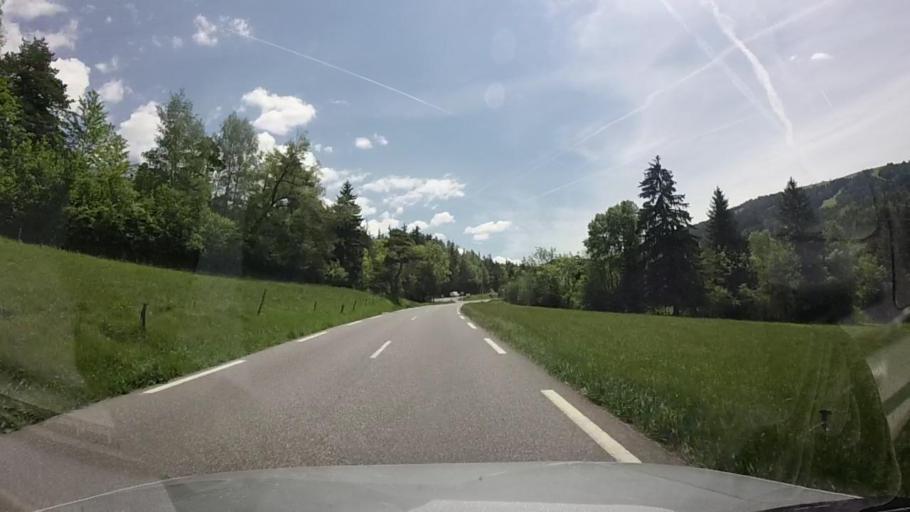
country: FR
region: Provence-Alpes-Cote d'Azur
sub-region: Departement des Alpes-de-Haute-Provence
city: Seyne-les-Alpes
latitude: 44.3330
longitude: 6.3901
